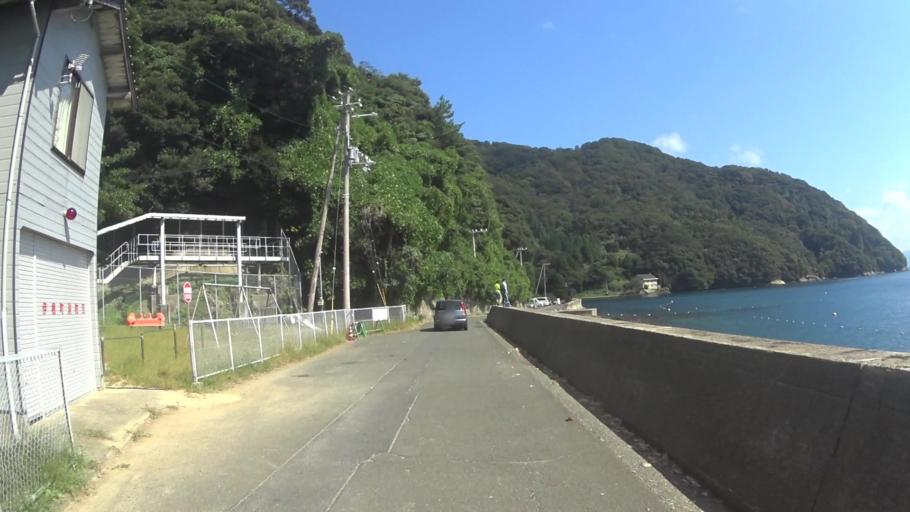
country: JP
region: Kyoto
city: Miyazu
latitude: 35.6645
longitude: 135.2880
